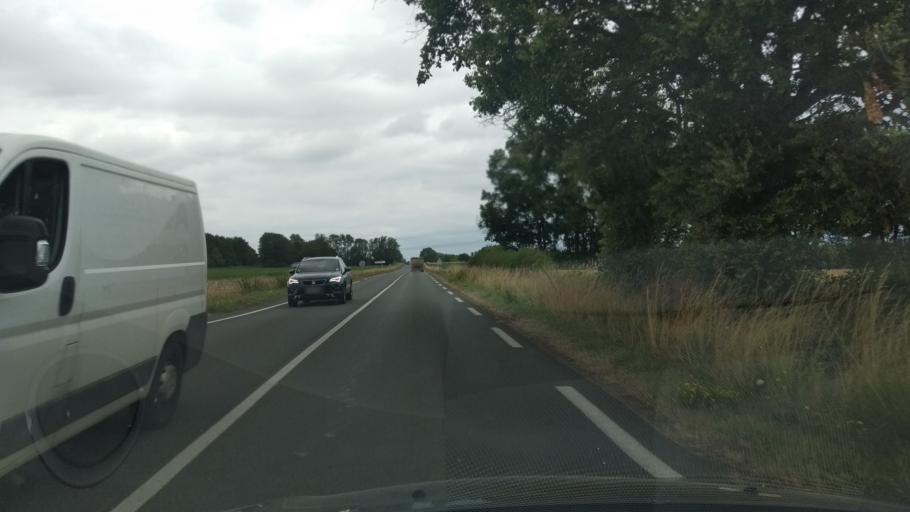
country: FR
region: Poitou-Charentes
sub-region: Departement de la Vienne
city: Saint-Maurice-la-Clouere
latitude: 46.3903
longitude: 0.4010
